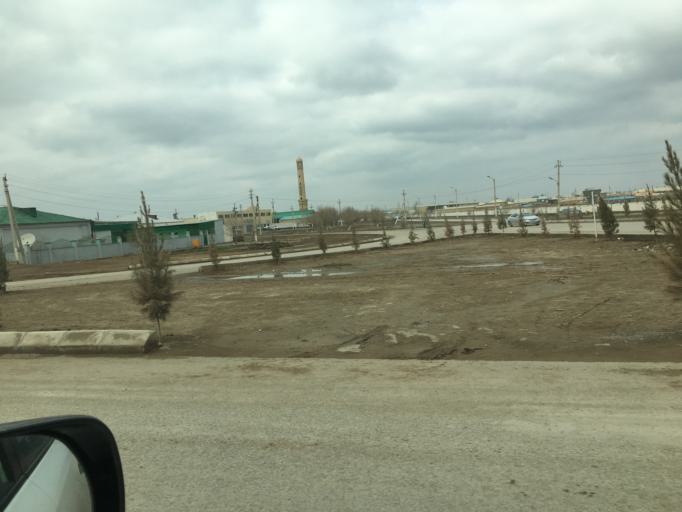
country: TM
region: Ahal
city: Tejen
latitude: 37.3755
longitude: 60.5171
